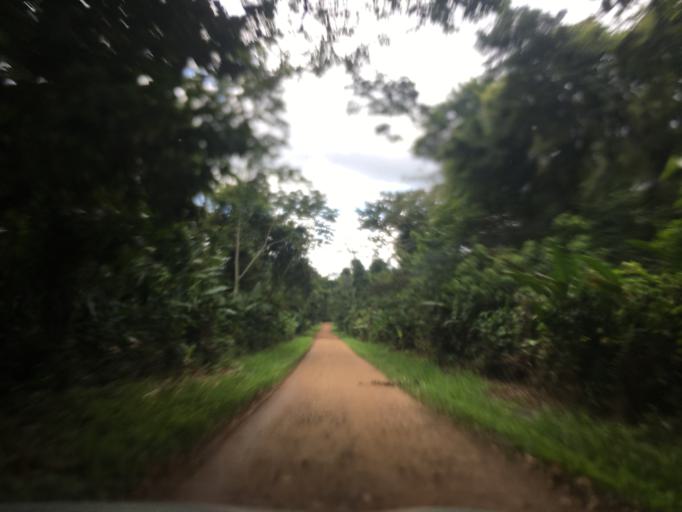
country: BZ
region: Stann Creek
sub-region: Dangriga
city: Dangriga
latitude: 16.9355
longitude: -88.3751
